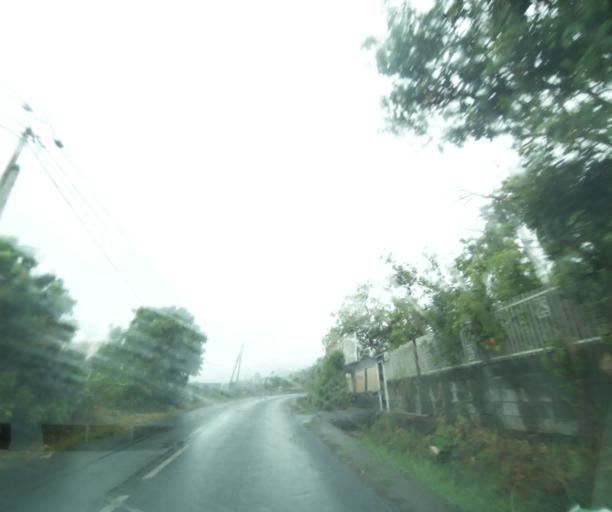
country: RE
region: Reunion
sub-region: Reunion
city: Saint-Paul
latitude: -21.0163
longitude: 55.3051
